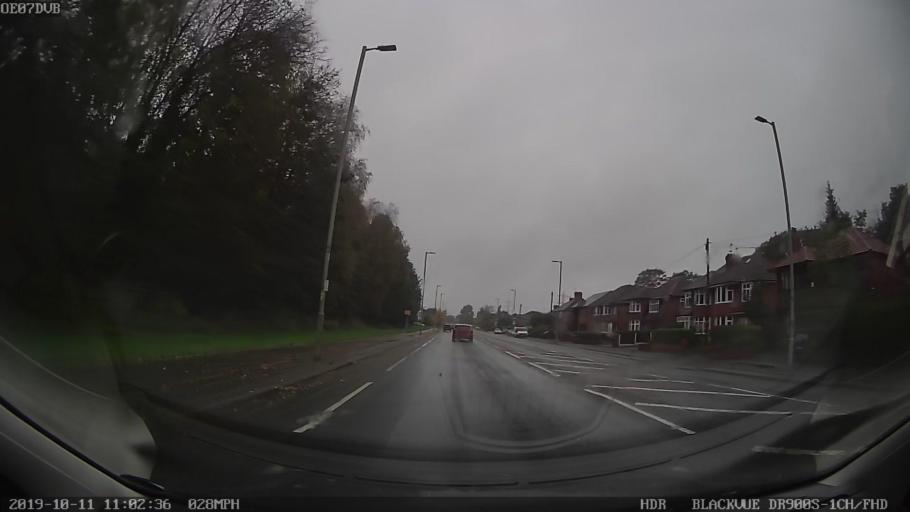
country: GB
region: England
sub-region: Borough of Rochdale
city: Middleton
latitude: 53.5299
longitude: -2.1932
